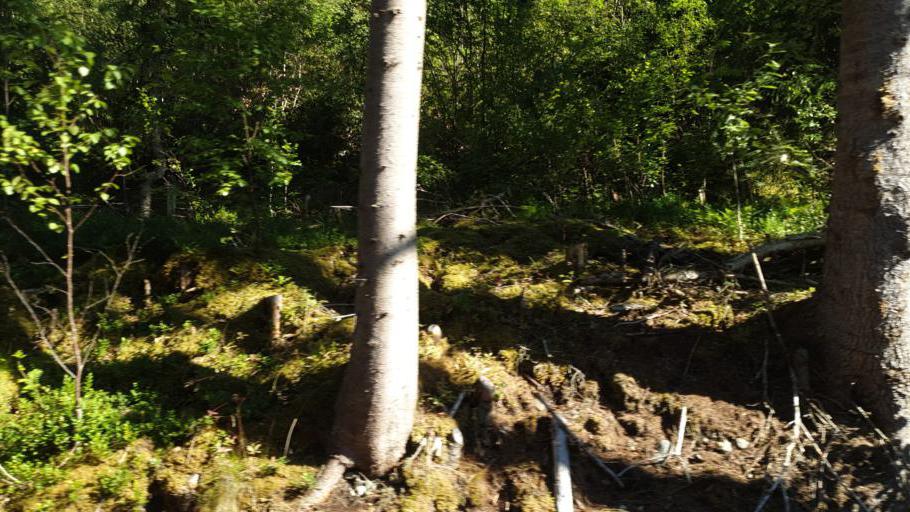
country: NO
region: Sor-Trondelag
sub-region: Orkdal
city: Orkanger
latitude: 63.1834
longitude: 9.7706
